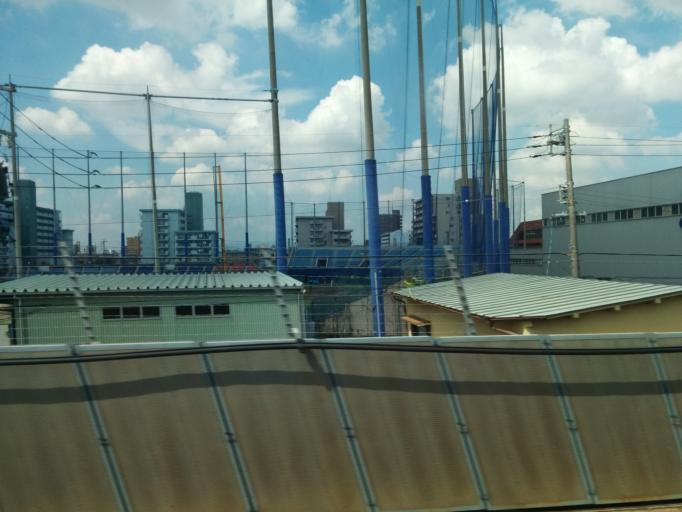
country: JP
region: Aichi
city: Nagoya-shi
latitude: 35.1477
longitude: 136.8880
